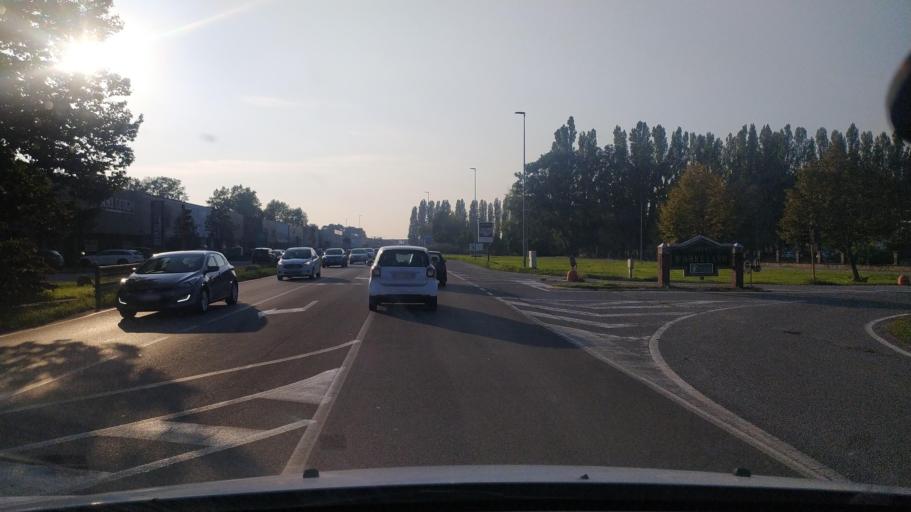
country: IT
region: Lombardy
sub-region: Provincia di Cremona
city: Capergnanica
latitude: 45.3597
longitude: 9.6519
